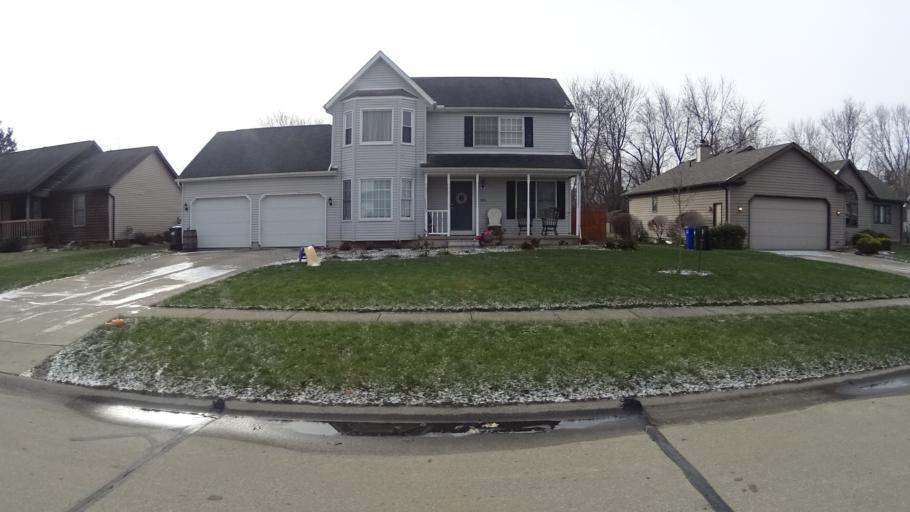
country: US
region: Ohio
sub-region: Lorain County
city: Lagrange
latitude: 41.2428
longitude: -82.1145
